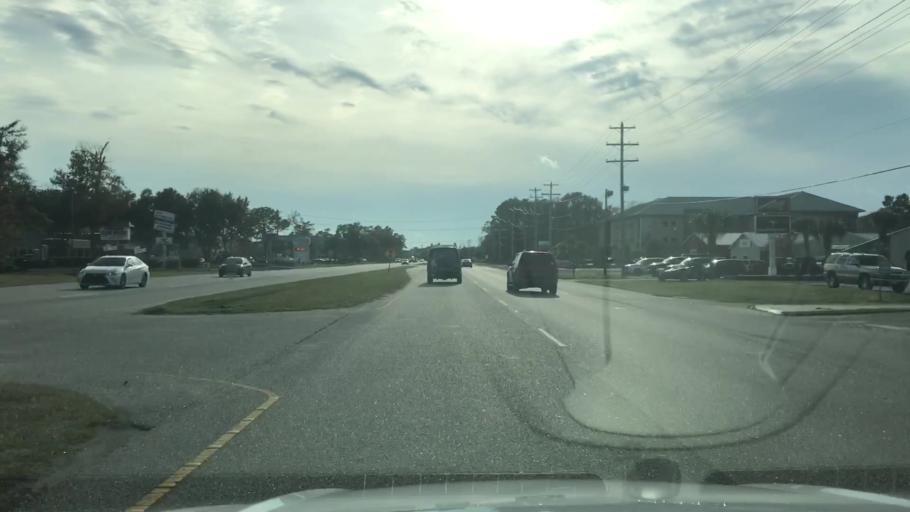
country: US
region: South Carolina
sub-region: Georgetown County
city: Murrells Inlet
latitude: 33.5626
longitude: -79.0387
